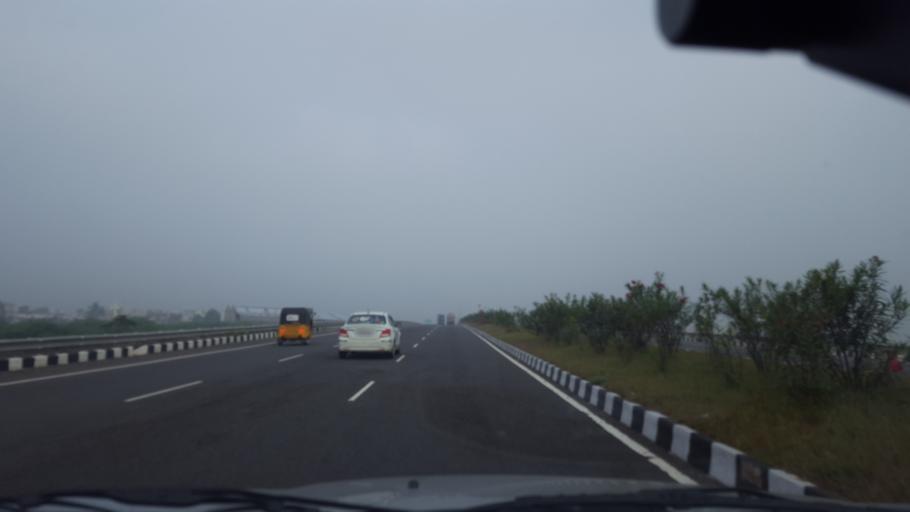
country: IN
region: Andhra Pradesh
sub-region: Prakasam
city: Ongole
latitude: 15.5265
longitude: 80.0590
